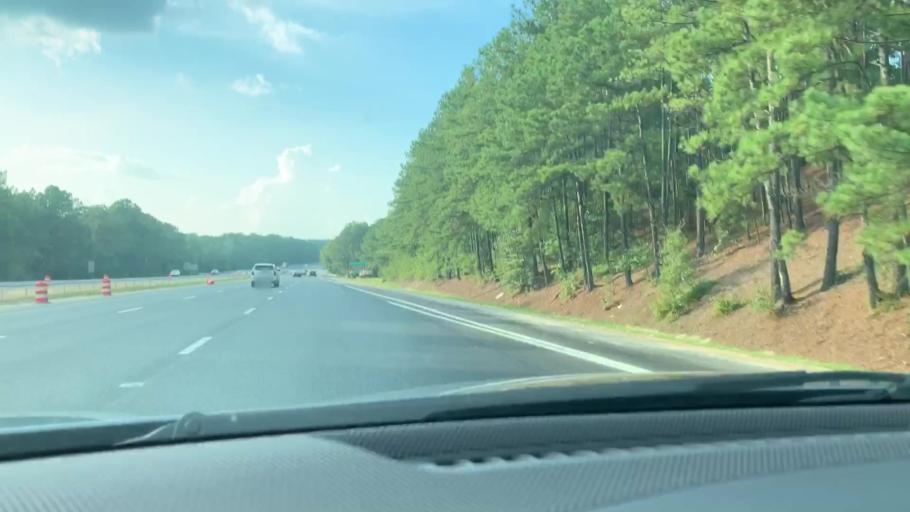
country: US
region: South Carolina
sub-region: Richland County
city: Dentsville
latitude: 34.0857
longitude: -80.9454
